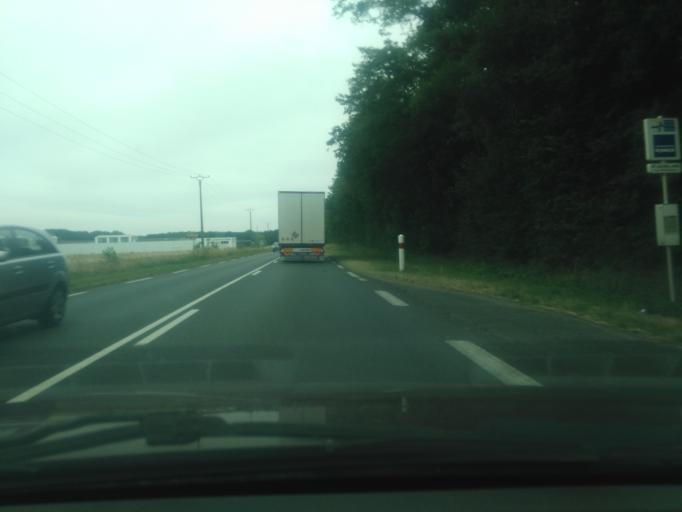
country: FR
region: Poitou-Charentes
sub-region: Departement de la Vienne
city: Lavoux
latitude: 46.5600
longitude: 0.5288
